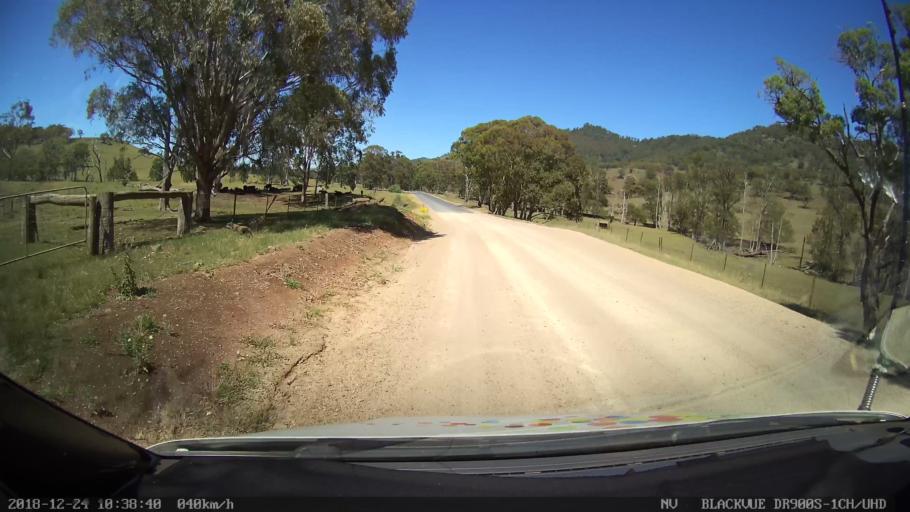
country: AU
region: New South Wales
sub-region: Upper Hunter Shire
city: Merriwa
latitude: -31.8492
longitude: 150.4808
